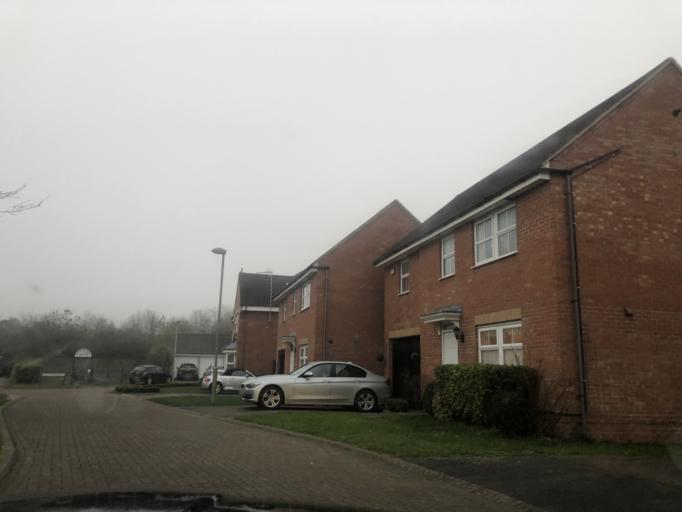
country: GB
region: England
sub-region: Oxfordshire
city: Bicester
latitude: 51.9107
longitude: -1.1675
